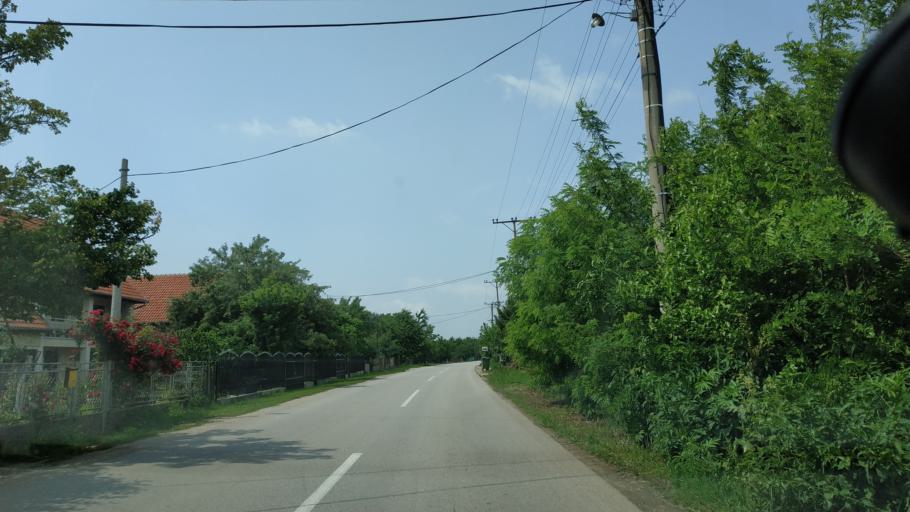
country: RS
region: Central Serbia
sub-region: Nisavski Okrug
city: Aleksinac
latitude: 43.4690
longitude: 21.7256
